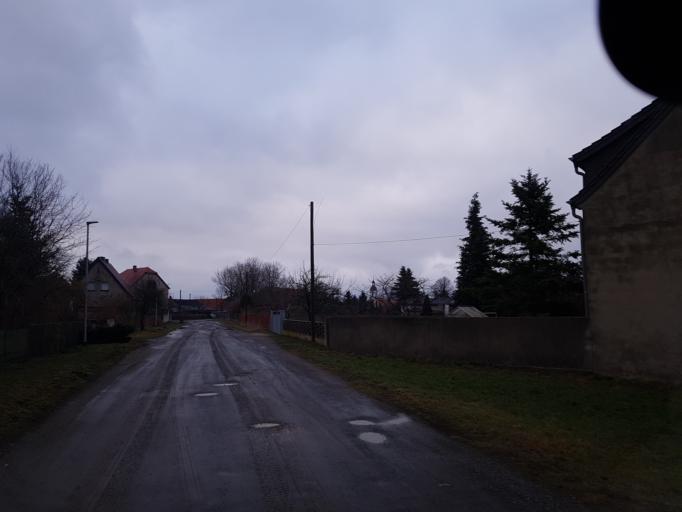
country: DE
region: Brandenburg
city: Plessa
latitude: 51.4613
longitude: 13.6150
